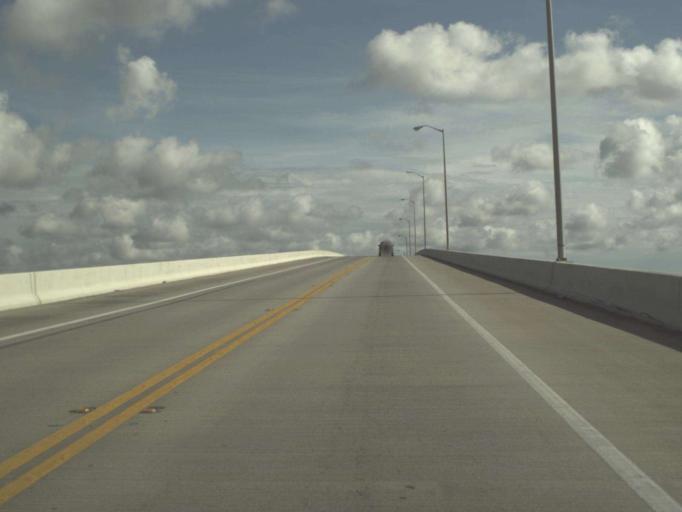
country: US
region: Florida
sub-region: Gulf County
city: Port Saint Joe
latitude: 29.8338
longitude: -85.3144
